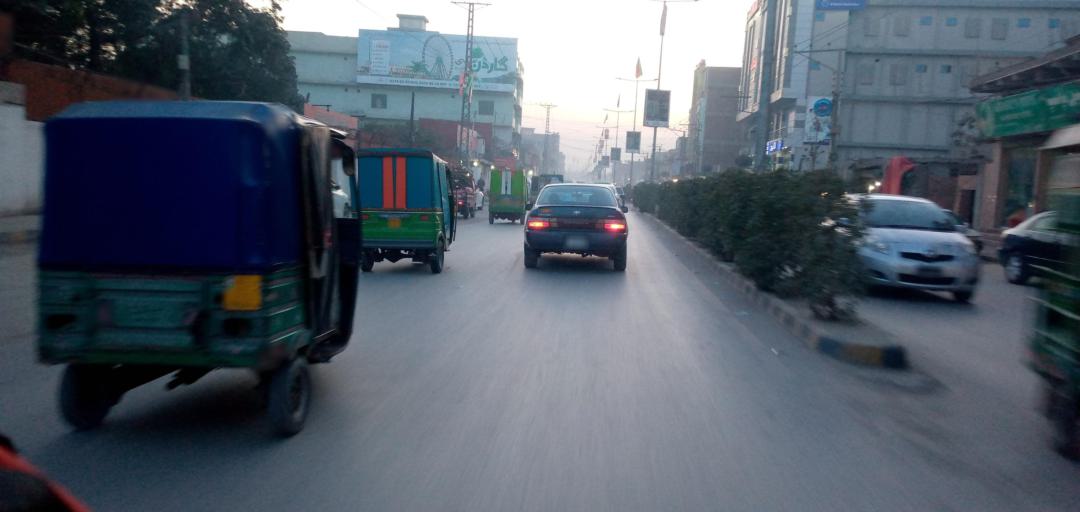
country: PK
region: Khyber Pakhtunkhwa
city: Peshawar
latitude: 34.0313
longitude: 71.6054
